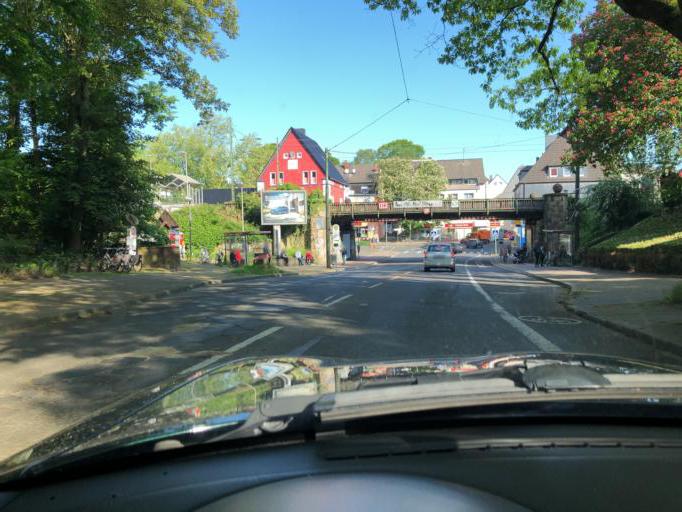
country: DE
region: North Rhine-Westphalia
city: Bochum-Hordel
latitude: 51.4595
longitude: 7.1553
